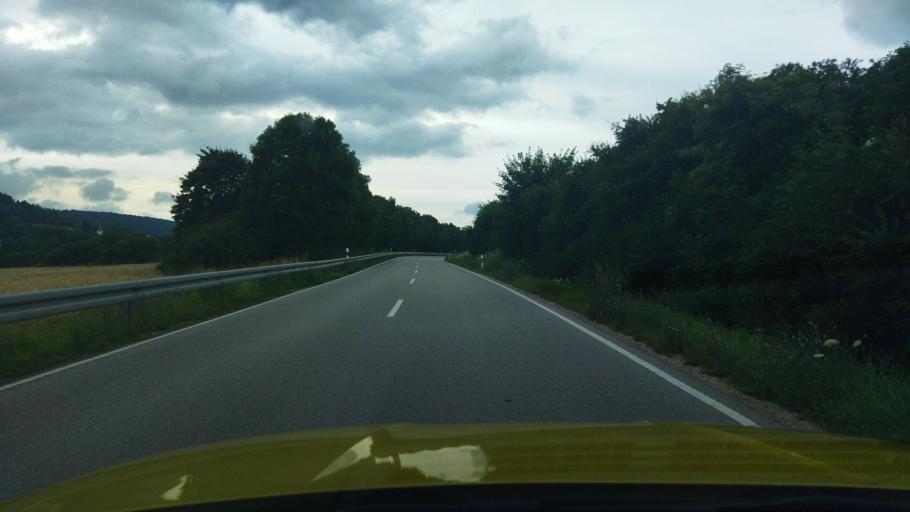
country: DE
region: Bavaria
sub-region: Regierungsbezirk Mittelfranken
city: Greding
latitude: 49.0590
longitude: 11.3329
